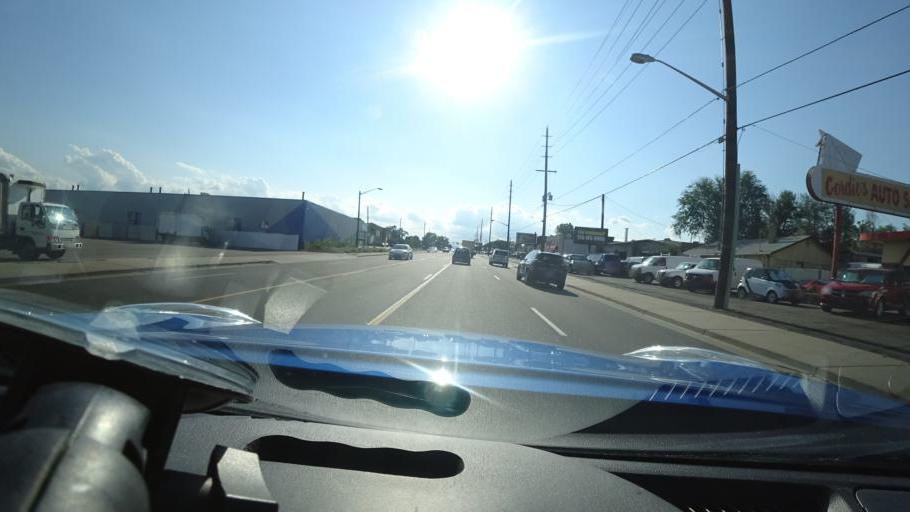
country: US
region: Colorado
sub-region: Arapahoe County
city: Sheridan
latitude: 39.6787
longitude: -105.0076
